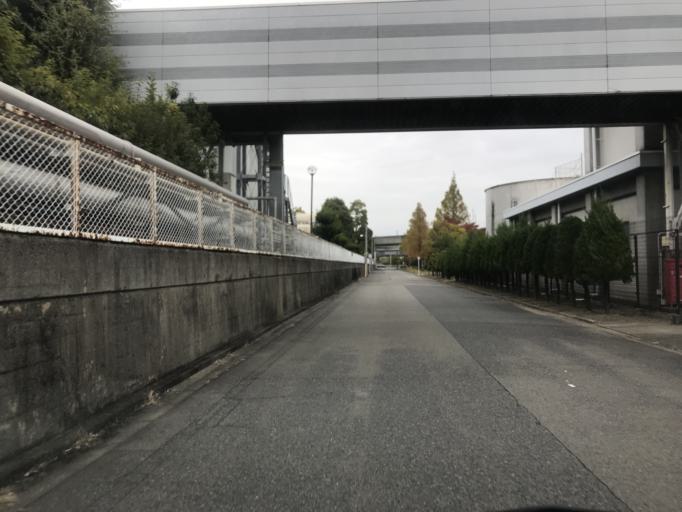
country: JP
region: Aichi
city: Nagoya-shi
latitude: 35.2078
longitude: 136.8528
